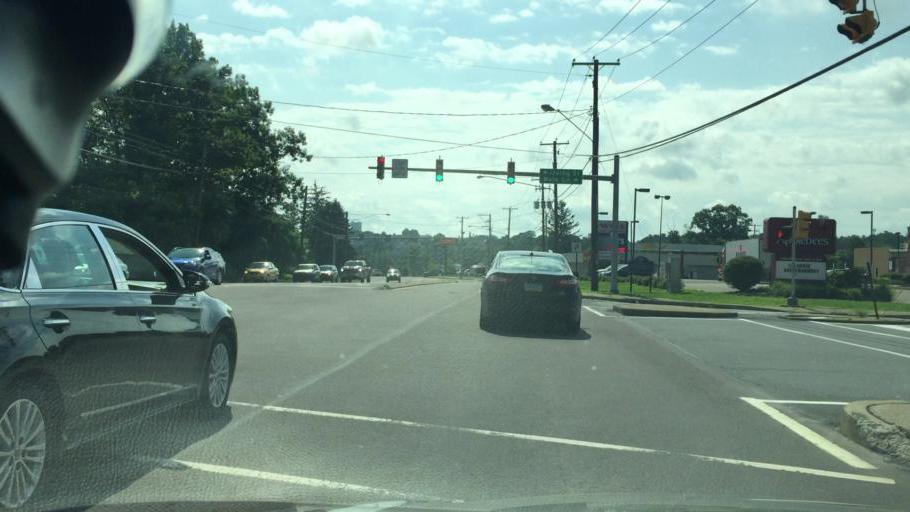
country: US
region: Pennsylvania
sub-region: Luzerne County
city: West Hazleton
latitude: 40.9680
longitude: -76.0049
